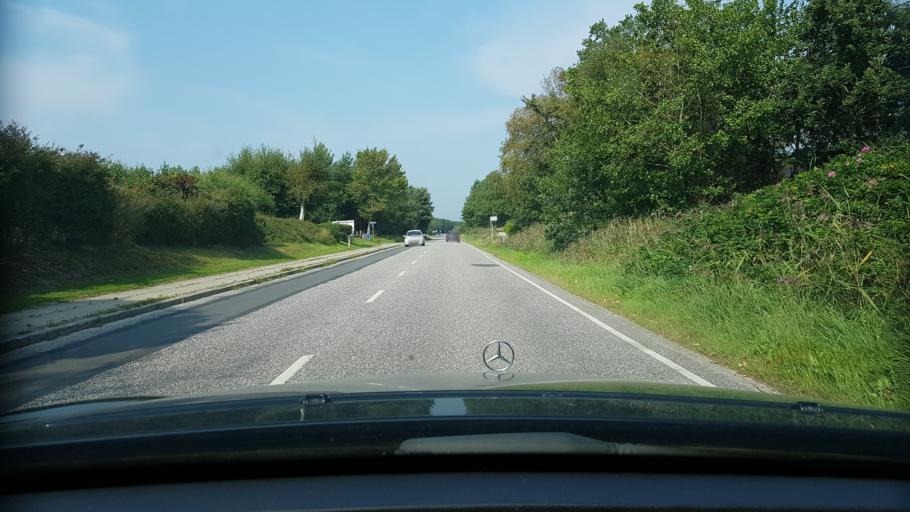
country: DK
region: North Denmark
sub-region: Alborg Kommune
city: Hals
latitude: 56.8181
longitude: 10.2706
